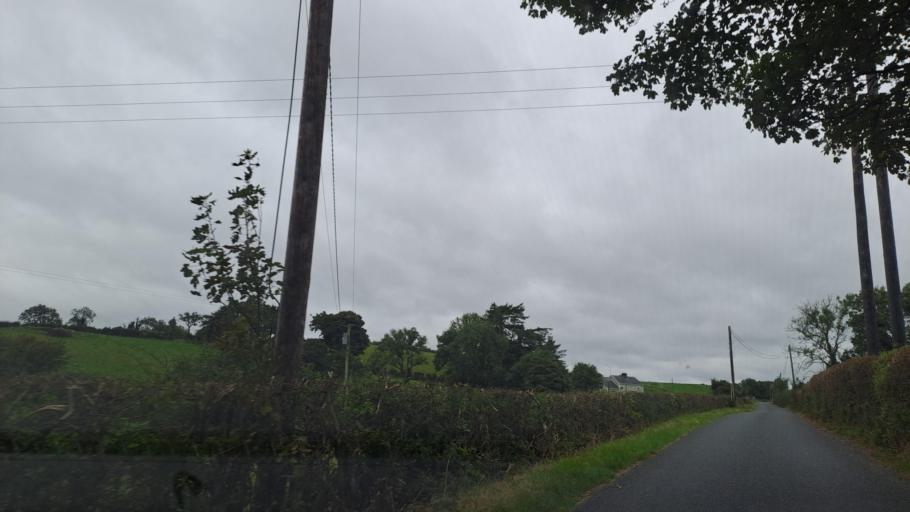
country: IE
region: Ulster
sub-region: An Cabhan
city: Kingscourt
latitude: 54.0096
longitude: -6.8772
